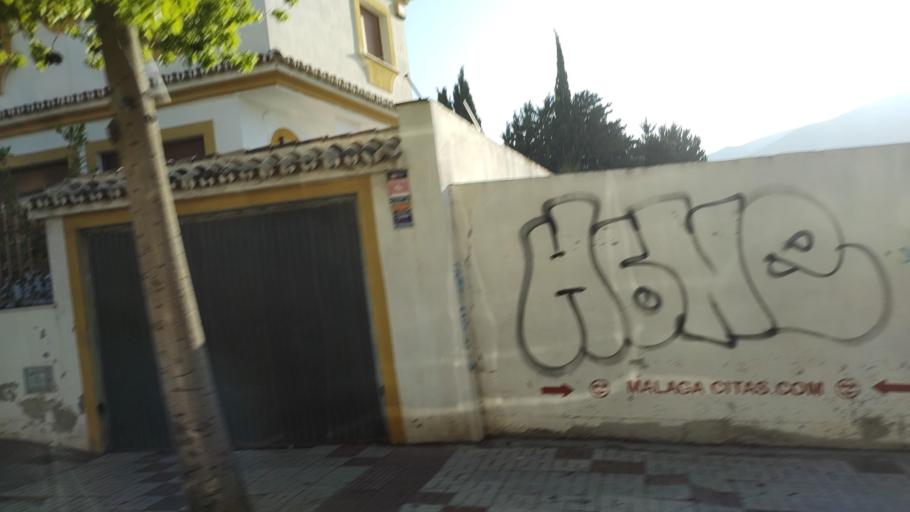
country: ES
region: Andalusia
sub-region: Provincia de Malaga
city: Torremolinos
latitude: 36.6305
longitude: -4.4993
